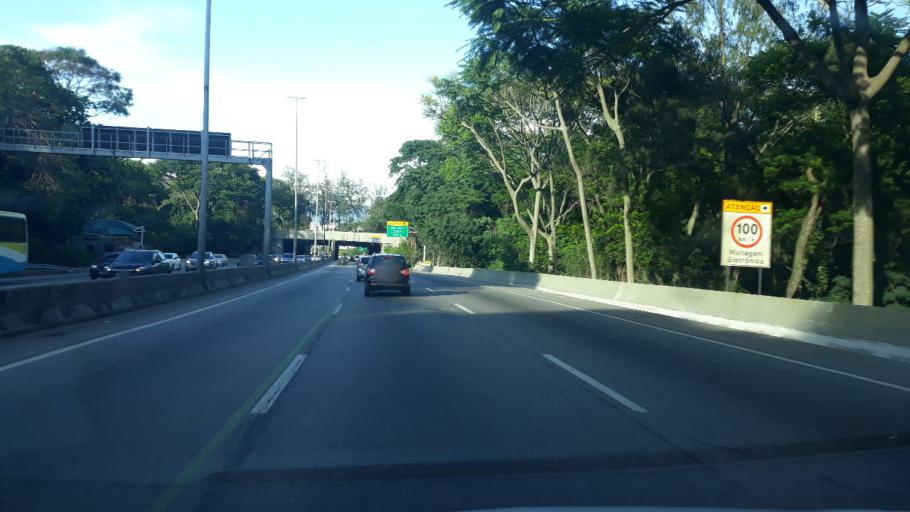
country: BR
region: Rio de Janeiro
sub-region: Sao Joao De Meriti
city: Sao Joao de Meriti
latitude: -22.9240
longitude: -43.3364
